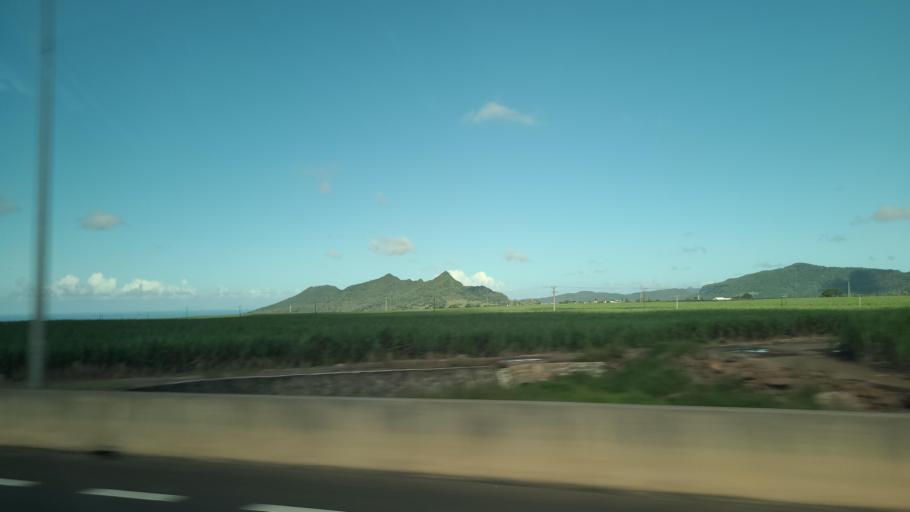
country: MU
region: Flacq
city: Camp de Masque
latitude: -20.2323
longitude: 57.6567
